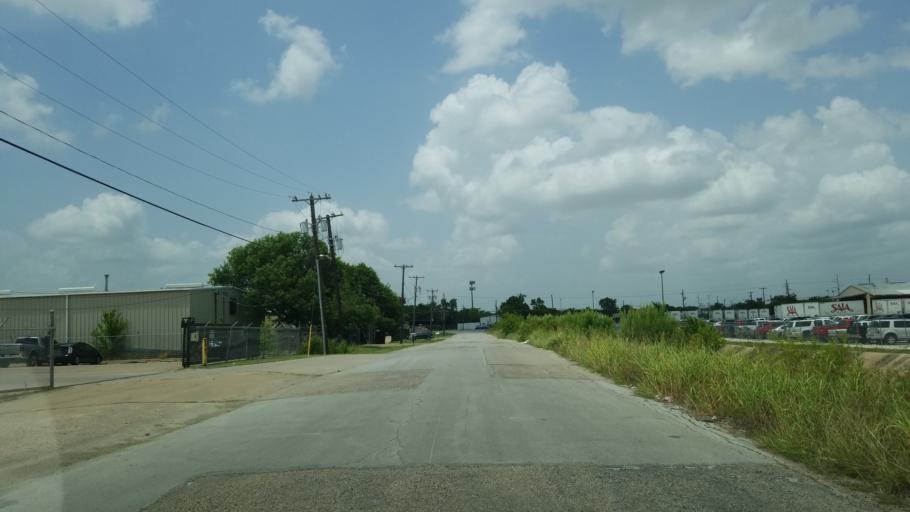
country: US
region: Texas
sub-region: Dallas County
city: Cockrell Hill
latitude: 32.7765
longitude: -96.8922
